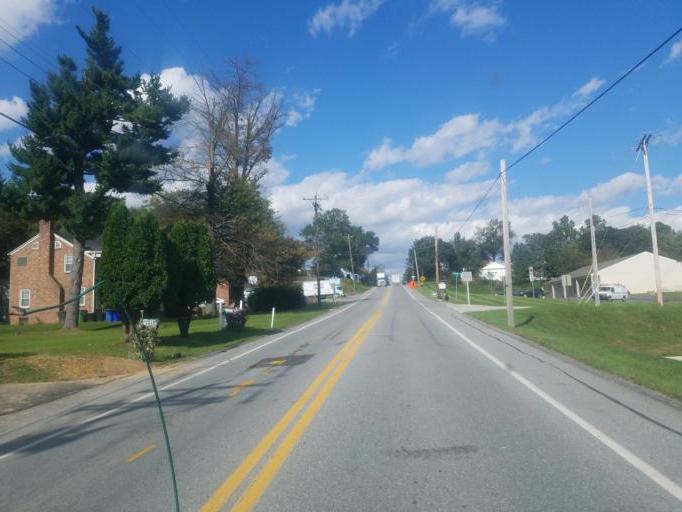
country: US
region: Pennsylvania
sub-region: York County
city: Emigsville
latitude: 40.0068
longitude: -76.7329
